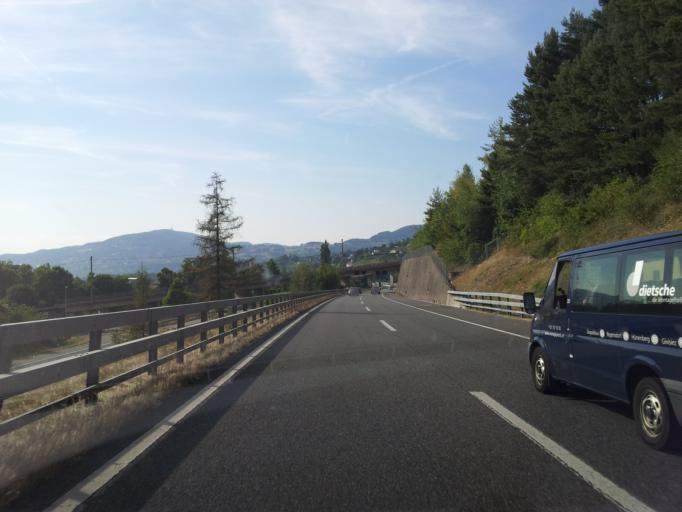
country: CH
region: Vaud
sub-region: Riviera-Pays-d'Enhaut District
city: Le Chatelard
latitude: 46.4466
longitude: 6.9028
